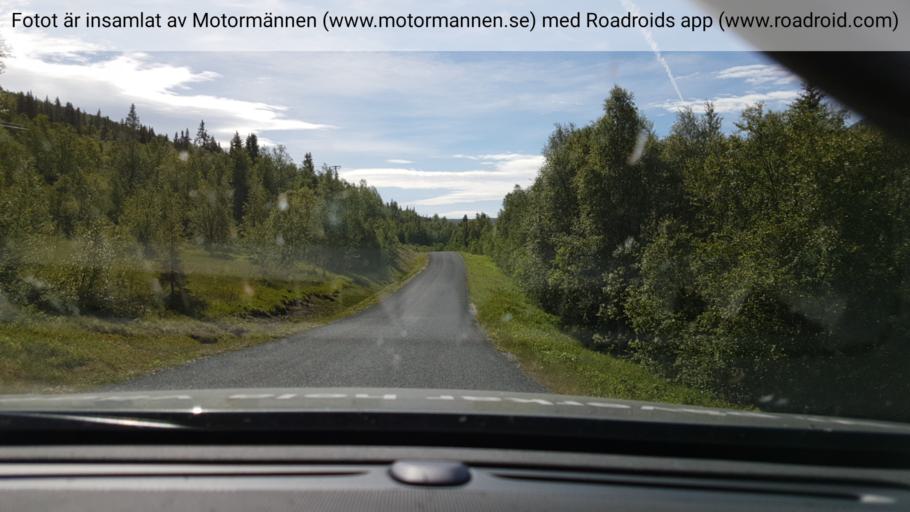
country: SE
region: Vaesterbotten
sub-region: Vilhelmina Kommun
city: Sjoberg
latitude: 65.3089
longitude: 15.2945
